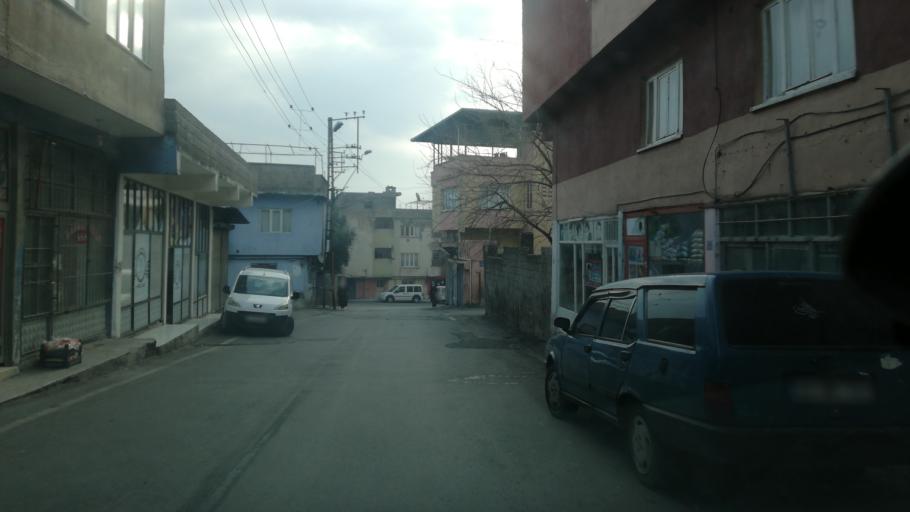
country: TR
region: Kahramanmaras
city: Kahramanmaras
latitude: 37.5895
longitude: 36.9112
